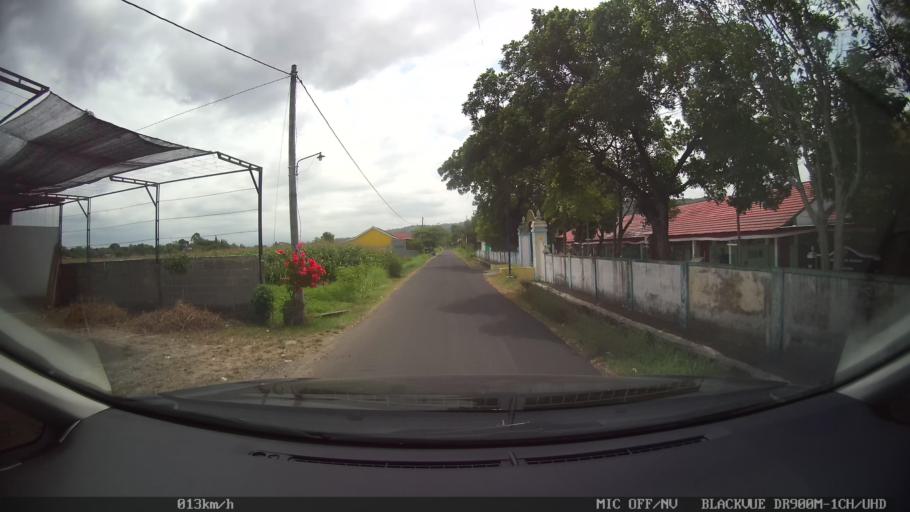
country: ID
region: Central Java
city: Candi Prambanan
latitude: -7.8148
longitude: 110.4999
